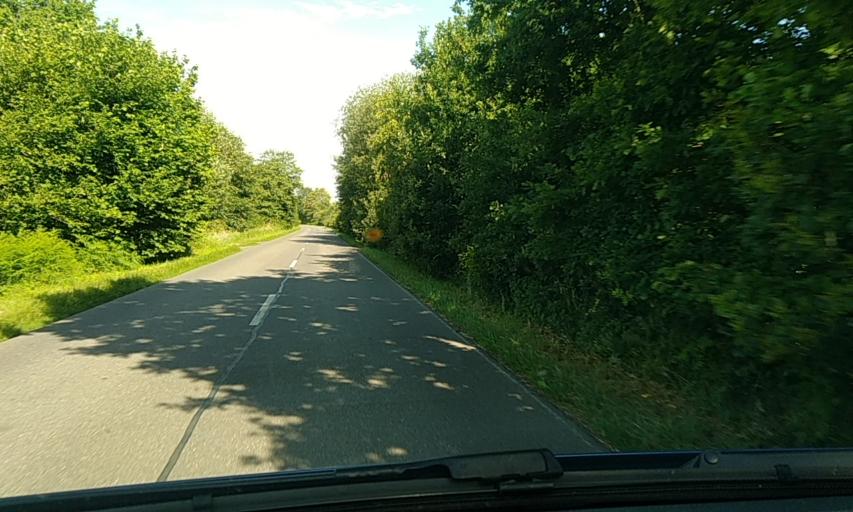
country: DE
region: Schleswig-Holstein
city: Fockbek
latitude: 54.2741
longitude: 9.5854
